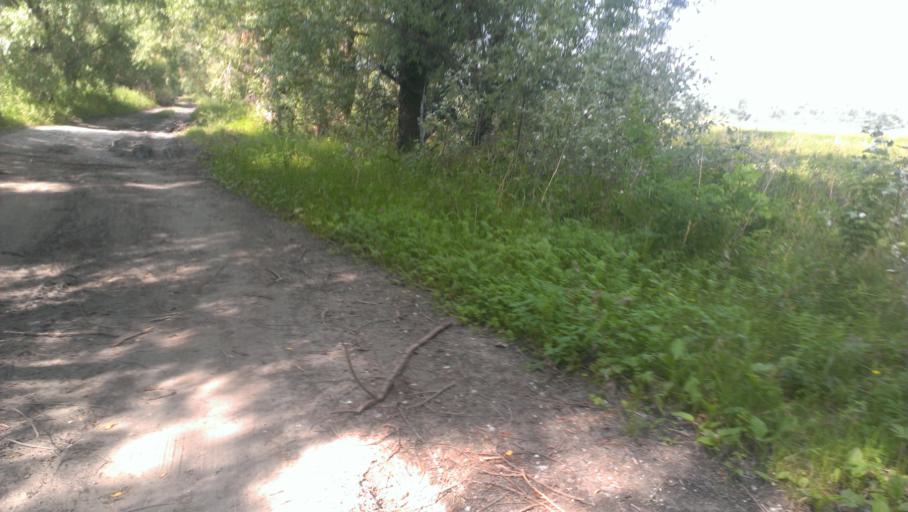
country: RU
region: Altai Krai
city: Novoaltaysk
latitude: 53.3743
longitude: 83.8569
